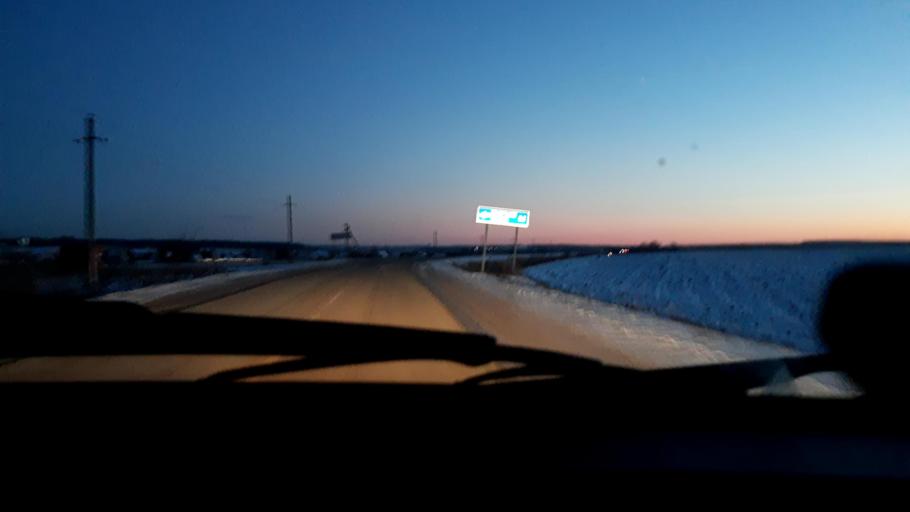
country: RU
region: Bashkortostan
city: Iglino
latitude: 54.7536
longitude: 56.3997
